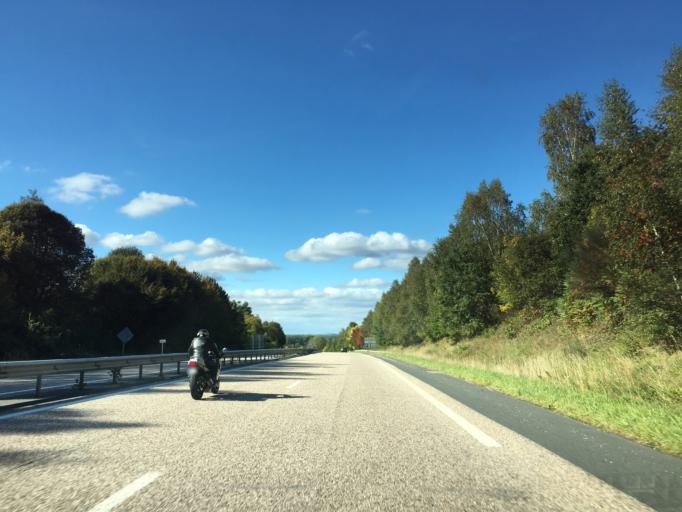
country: FR
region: Lorraine
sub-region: Departement de Meurthe-et-Moselle
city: Baccarat
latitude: 48.4636
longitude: 6.7443
